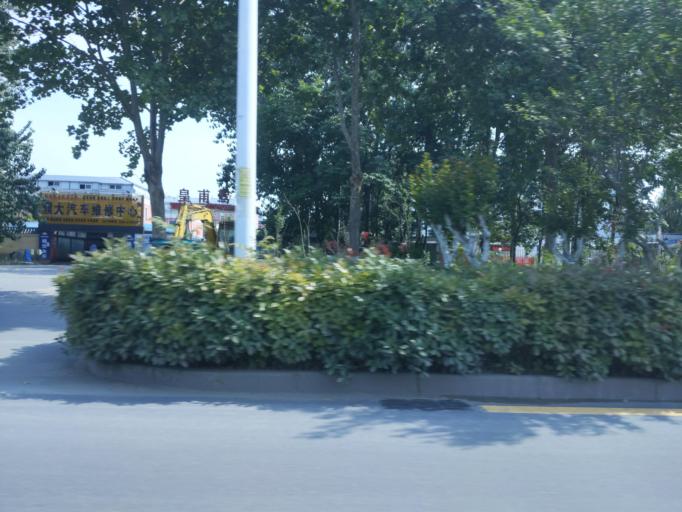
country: CN
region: Henan Sheng
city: Puyang
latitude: 35.7744
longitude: 114.9536
